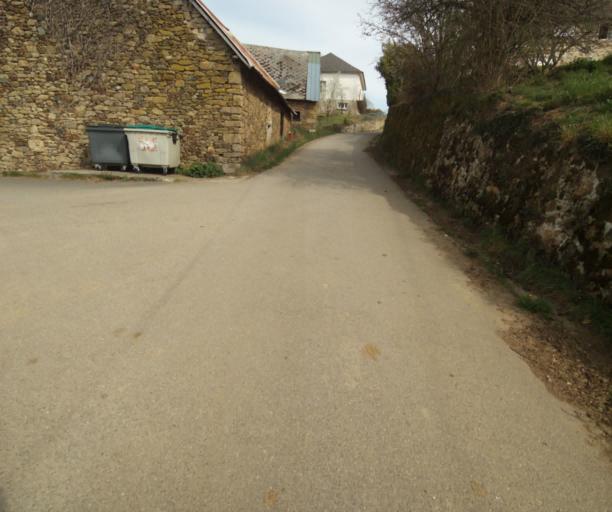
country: FR
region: Limousin
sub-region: Departement de la Correze
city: Correze
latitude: 45.3593
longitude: 1.8157
